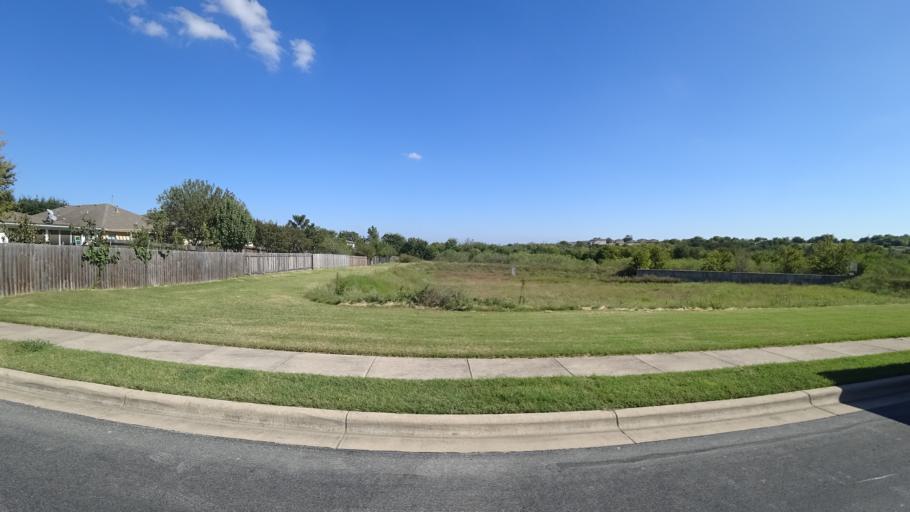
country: US
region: Texas
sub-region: Travis County
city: Manor
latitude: 30.3621
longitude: -97.6090
